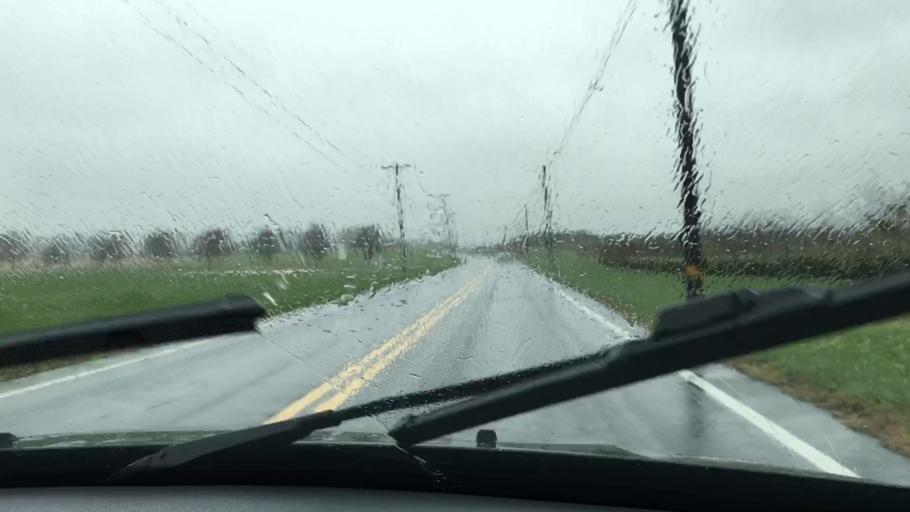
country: US
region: Maryland
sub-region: Frederick County
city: Adamstown
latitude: 39.2870
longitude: -77.4594
